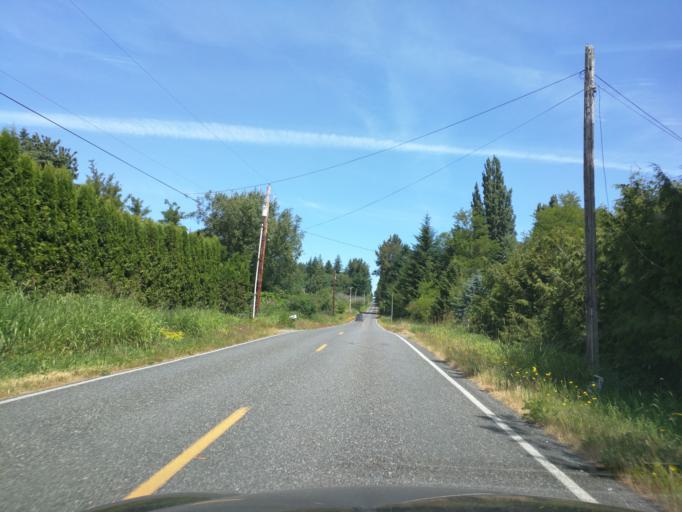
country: US
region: Washington
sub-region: Whatcom County
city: Geneva
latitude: 48.8163
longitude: -122.3989
